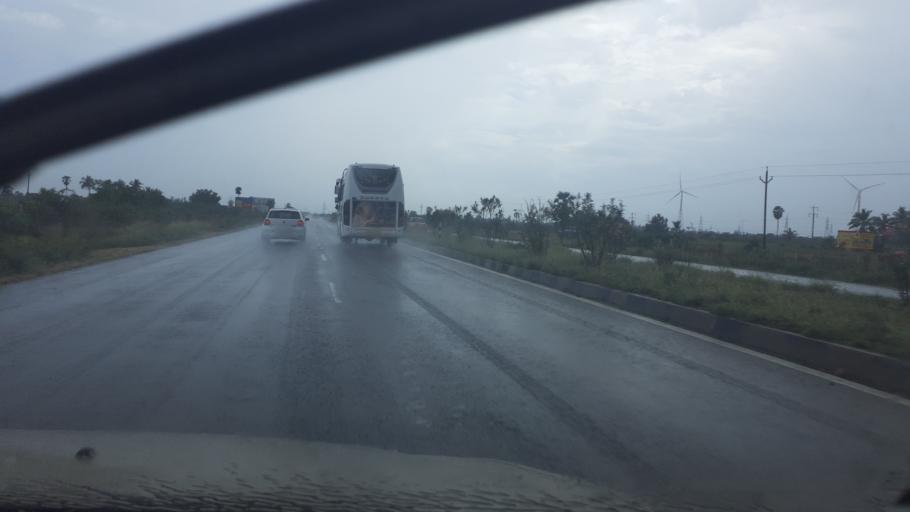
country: IN
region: Tamil Nadu
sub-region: Thoothukkudi
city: Kayattar
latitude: 8.9182
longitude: 77.7653
